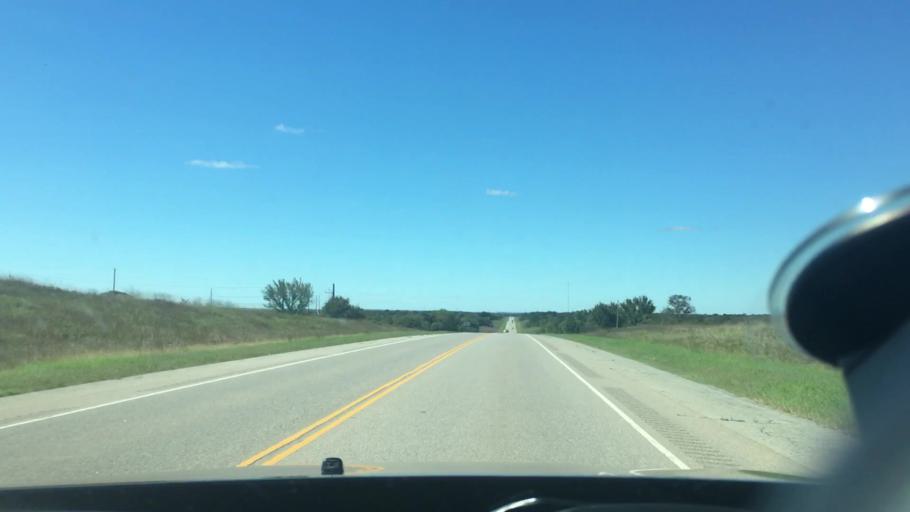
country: US
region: Oklahoma
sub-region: Coal County
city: Coalgate
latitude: 34.6191
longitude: -96.4508
